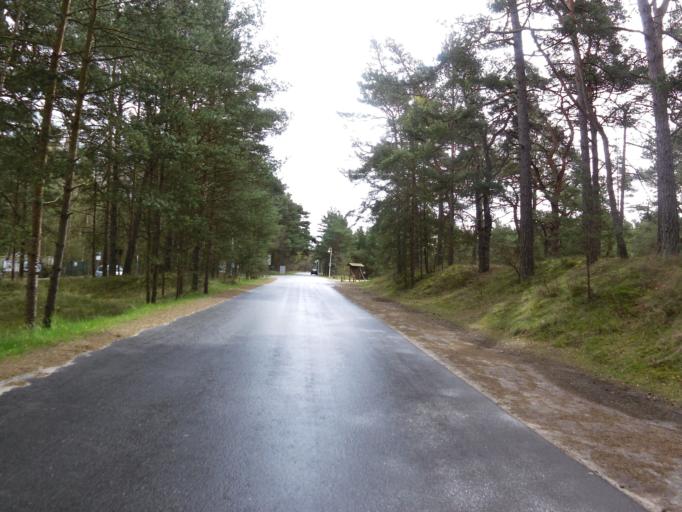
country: DE
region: Mecklenburg-Vorpommern
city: Ostseebad Prerow
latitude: 54.4543
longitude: 12.5471
